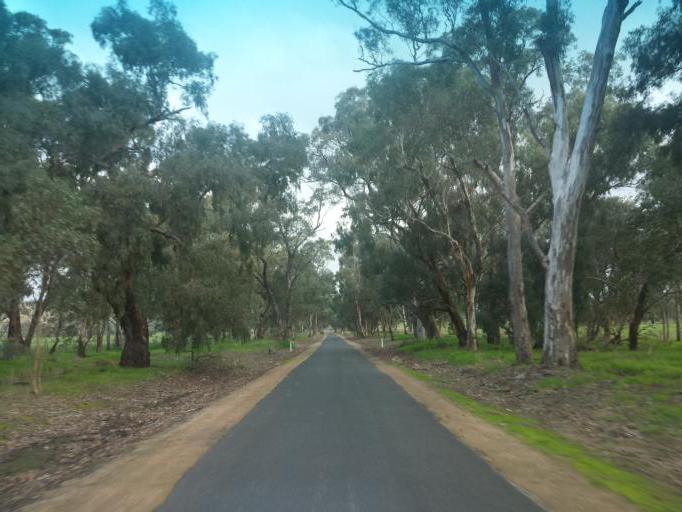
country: AU
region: Victoria
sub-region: Murrindindi
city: Kinglake West
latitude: -36.9233
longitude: 145.2245
